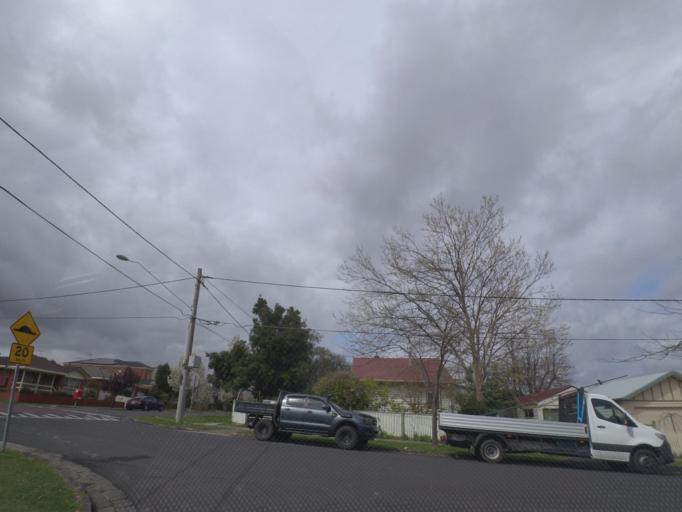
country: AU
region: Victoria
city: Mitcham
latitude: -37.8142
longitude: 145.1892
